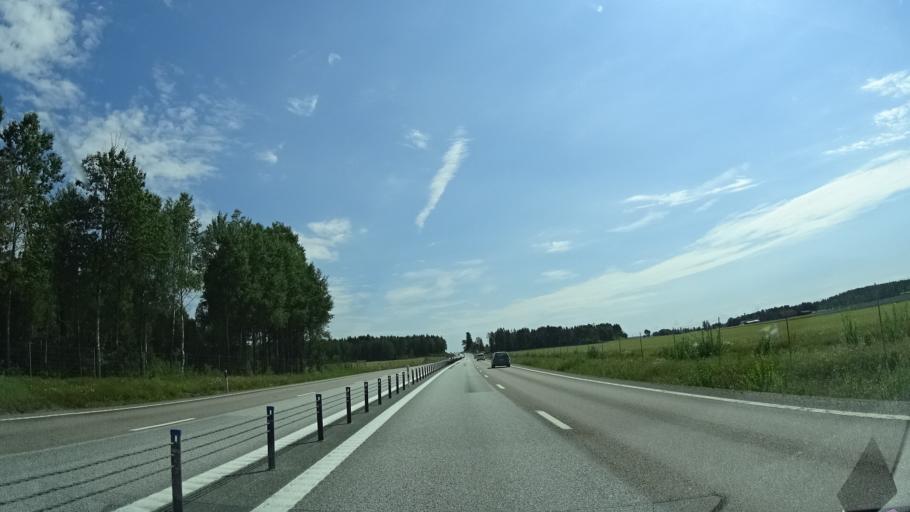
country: SE
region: Vaermland
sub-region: Kristinehamns Kommun
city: Kristinehamn
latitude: 59.3783
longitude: 13.9156
